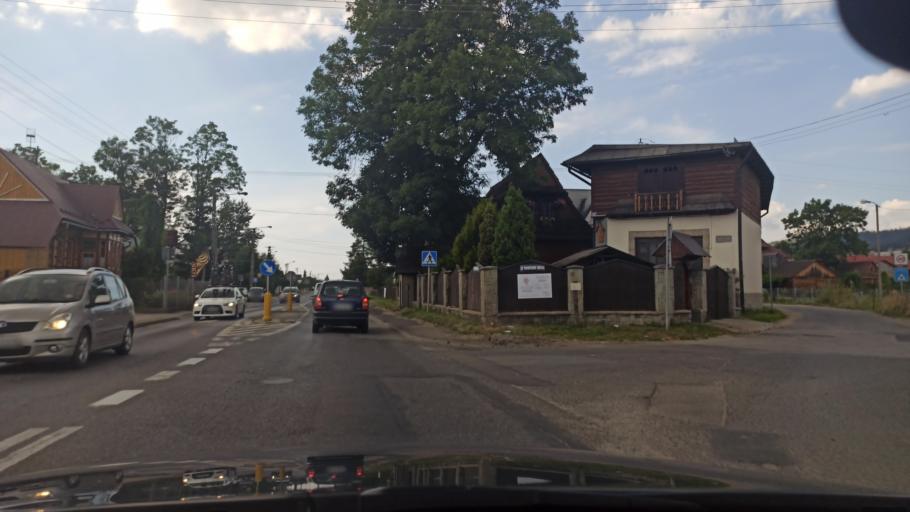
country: PL
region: Lesser Poland Voivodeship
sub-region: Powiat nowotarski
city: Ostrowsko
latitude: 49.4763
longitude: 20.0974
